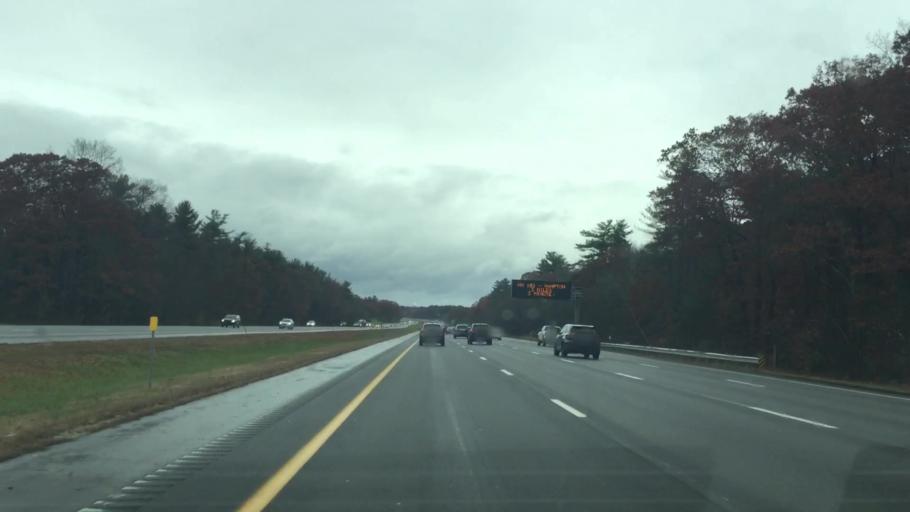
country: US
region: New Hampshire
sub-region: Rockingham County
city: Hampton Falls
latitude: 42.9221
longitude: -70.8687
